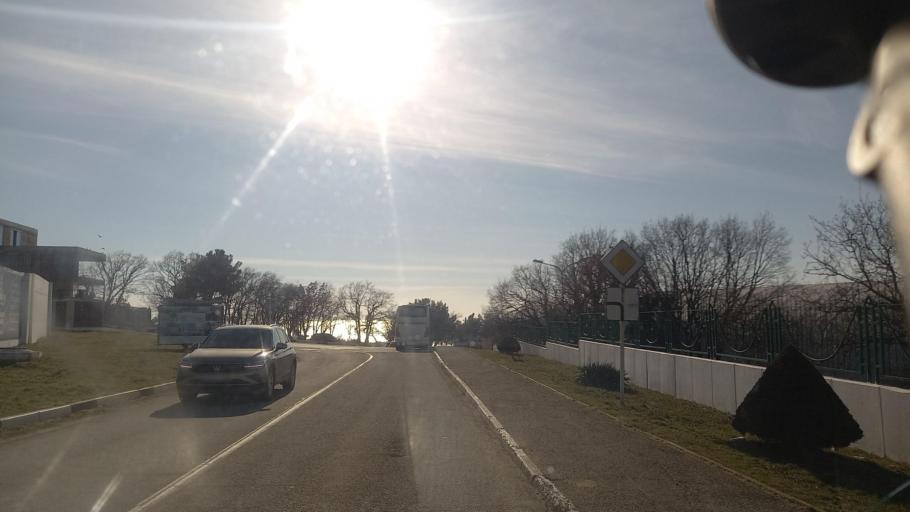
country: RU
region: Krasnodarskiy
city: Kabardinka
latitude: 44.6311
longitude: 37.9083
